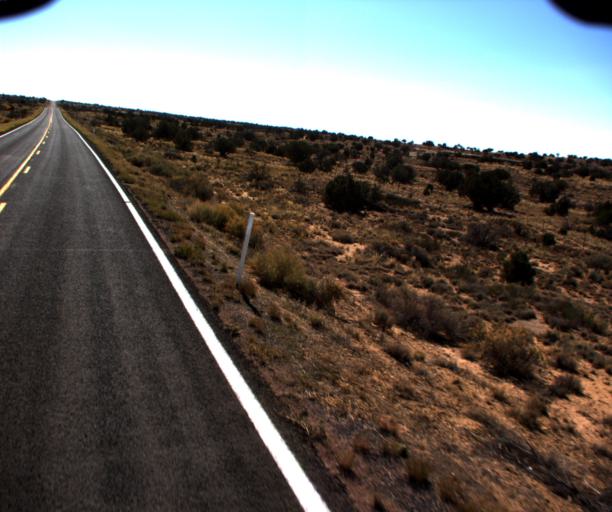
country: US
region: Arizona
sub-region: Coconino County
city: Tuba City
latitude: 35.9572
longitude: -110.8525
